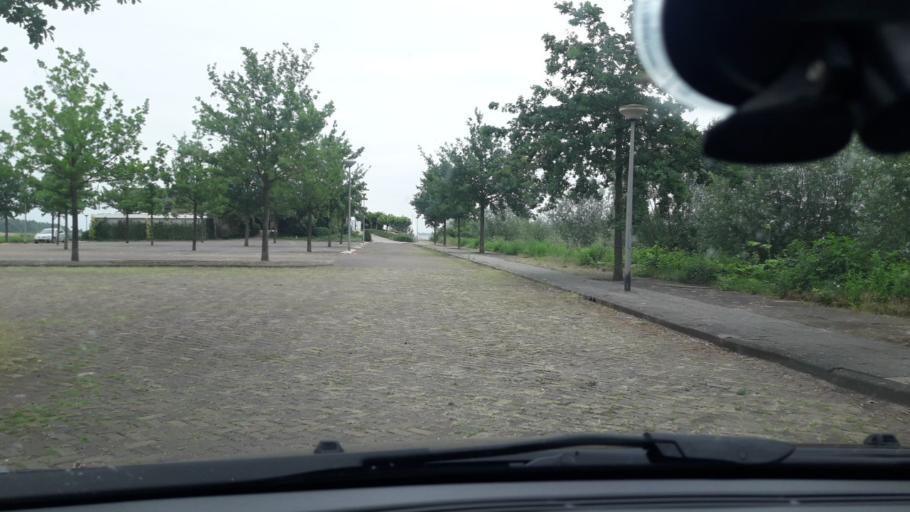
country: NL
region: Flevoland
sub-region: Gemeente Dronten
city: Dronten
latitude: 52.5800
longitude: 5.7608
